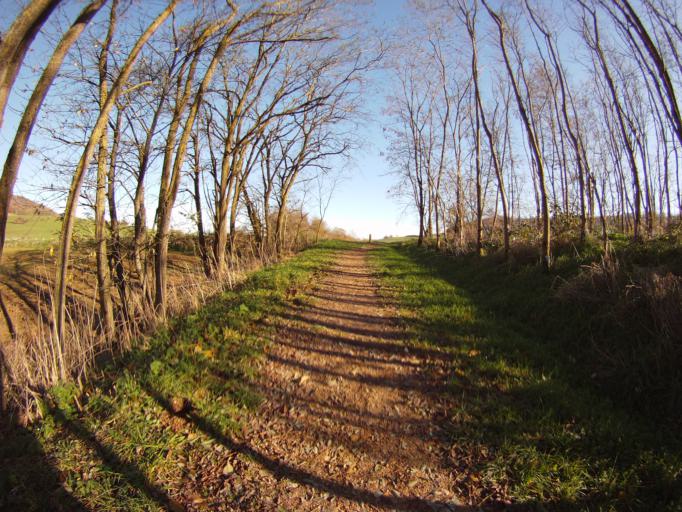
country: FR
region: Lorraine
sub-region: Departement de Meurthe-et-Moselle
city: Bouxieres-aux-Chenes
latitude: 48.7967
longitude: 6.2417
